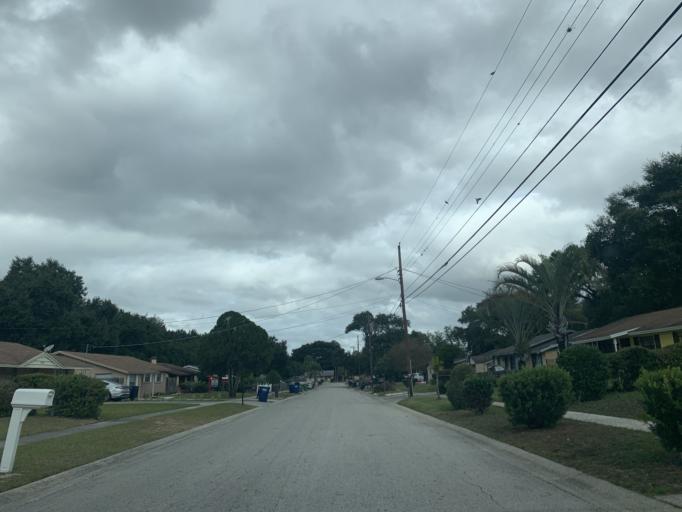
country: US
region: Florida
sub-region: Hillsborough County
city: East Lake-Orient Park
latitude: 27.9855
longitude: -82.4045
